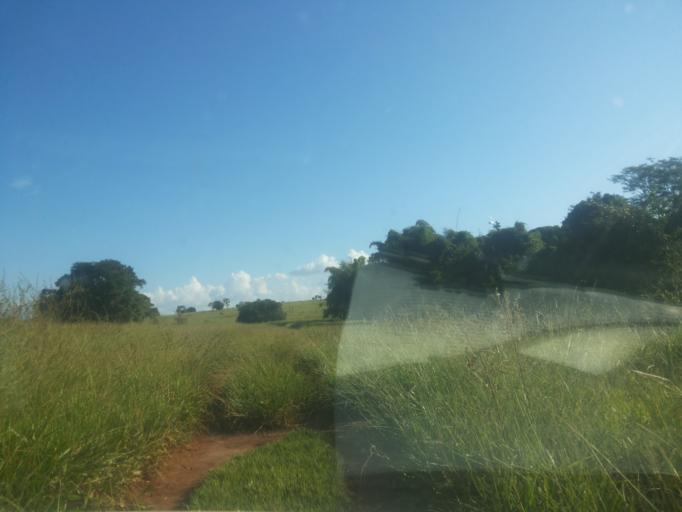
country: BR
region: Minas Gerais
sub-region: Santa Vitoria
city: Santa Vitoria
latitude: -19.0002
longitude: -50.4474
